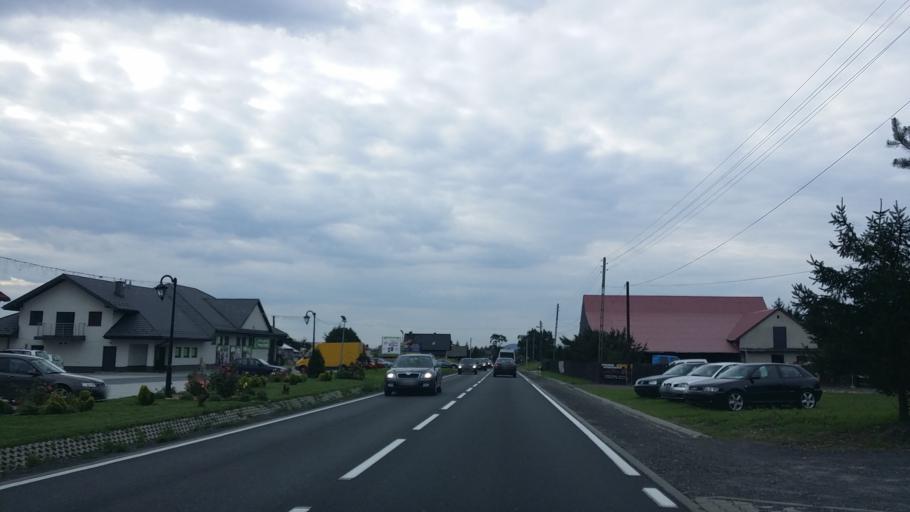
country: PL
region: Lesser Poland Voivodeship
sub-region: Powiat wadowicki
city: Spytkowice
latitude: 49.9936
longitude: 19.5167
